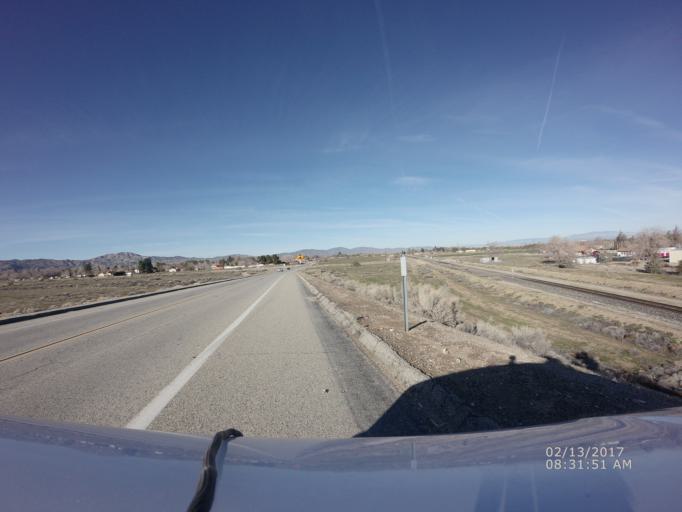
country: US
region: California
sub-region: Los Angeles County
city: Littlerock
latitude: 34.5432
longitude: -117.9555
